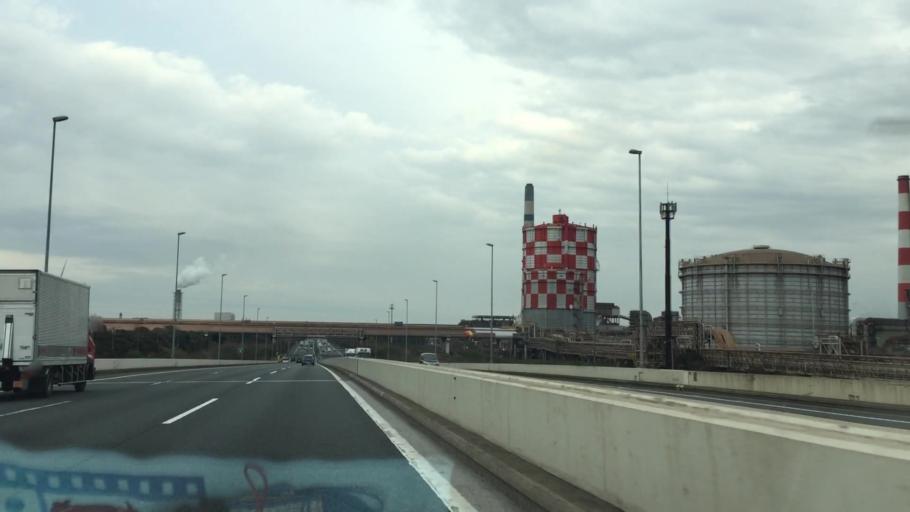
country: JP
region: Kanagawa
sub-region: Kawasaki-shi
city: Kawasaki
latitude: 35.4820
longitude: 139.7186
